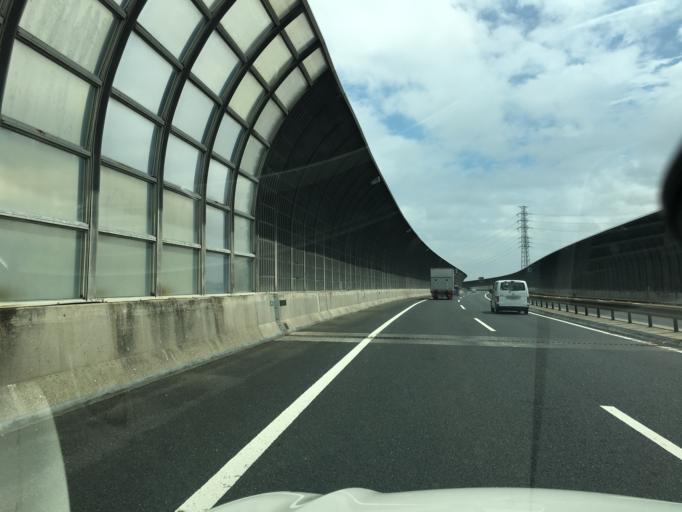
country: JP
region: Saitama
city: Shimotoda
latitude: 35.8366
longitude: 139.6687
